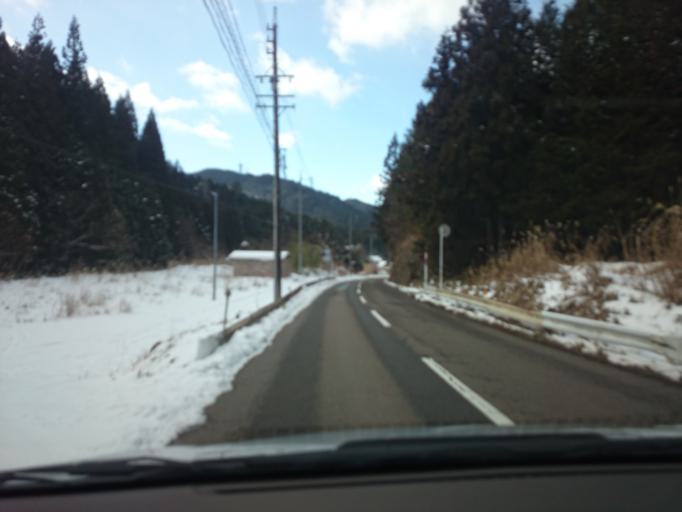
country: JP
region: Gifu
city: Gujo
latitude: 35.7393
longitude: 137.0162
